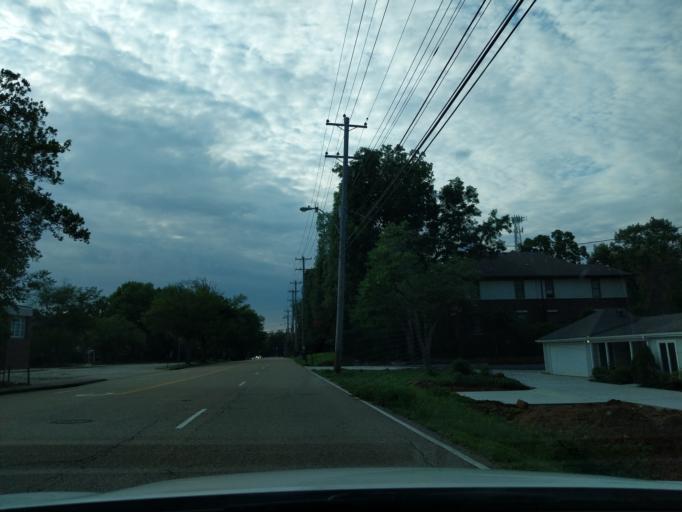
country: US
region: Tennessee
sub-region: Shelby County
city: Germantown
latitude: 35.0828
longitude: -89.8066
